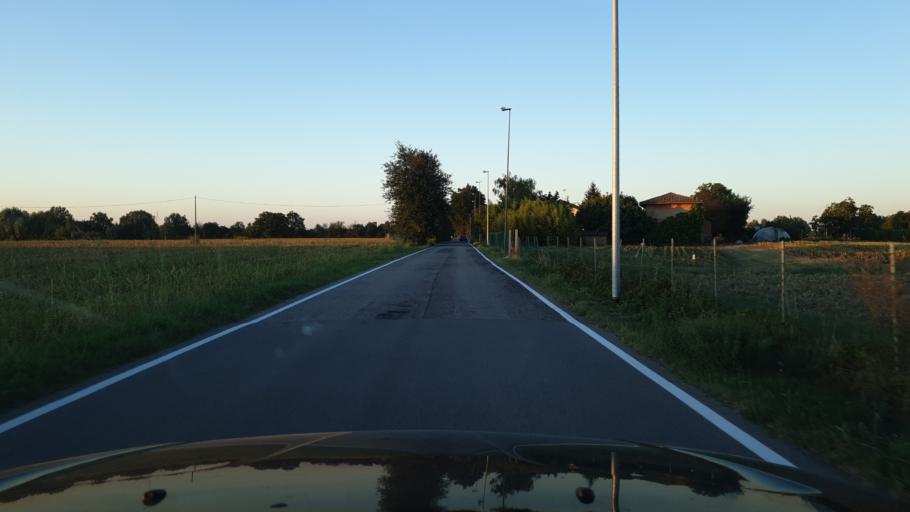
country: IT
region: Emilia-Romagna
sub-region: Provincia di Bologna
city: Quarto Inferiore
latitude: 44.5222
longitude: 11.3911
